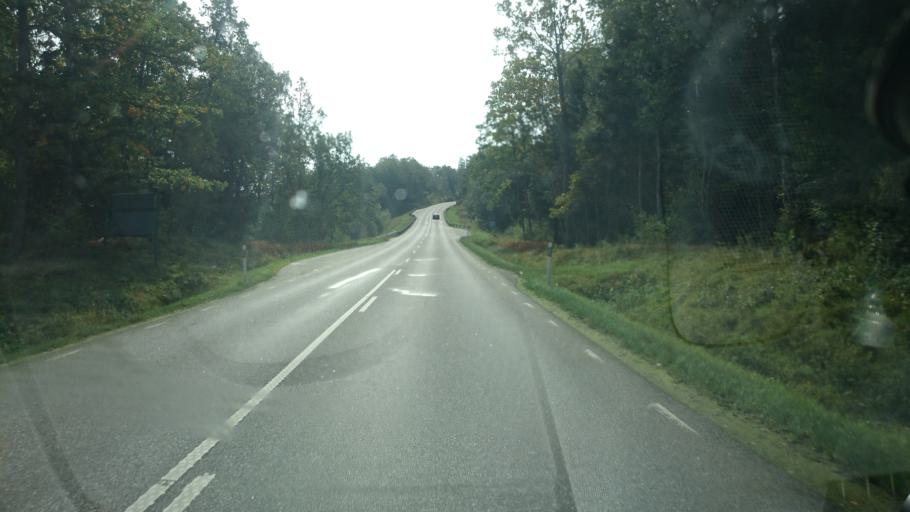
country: SE
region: Vaestra Goetaland
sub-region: Alingsas Kommun
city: Sollebrunn
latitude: 58.0538
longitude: 12.4666
